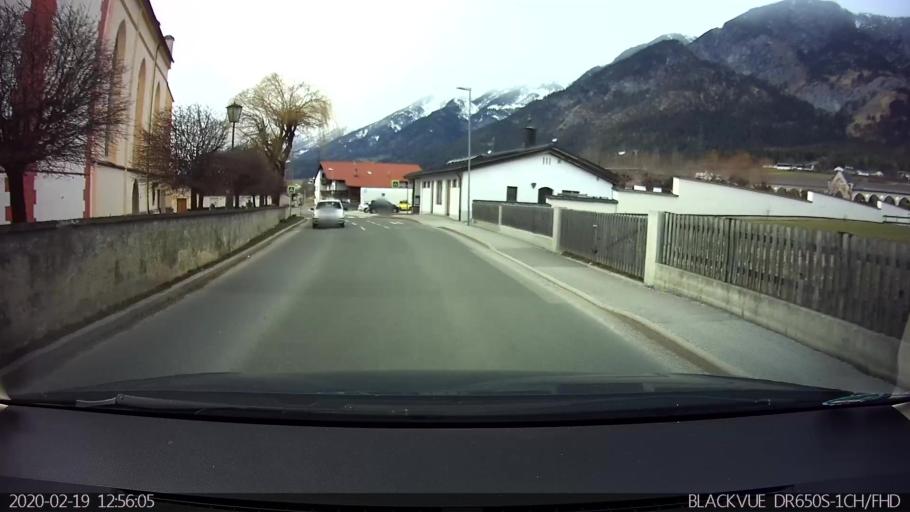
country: AT
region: Tyrol
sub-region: Politischer Bezirk Innsbruck Land
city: Absam
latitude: 47.2959
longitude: 11.5018
